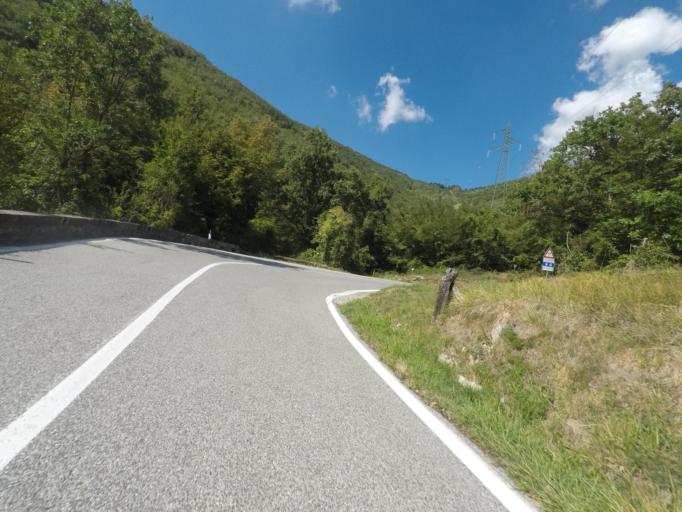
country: IT
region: Tuscany
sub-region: Provincia di Massa-Carrara
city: Fivizzano
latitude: 44.2582
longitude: 10.1723
